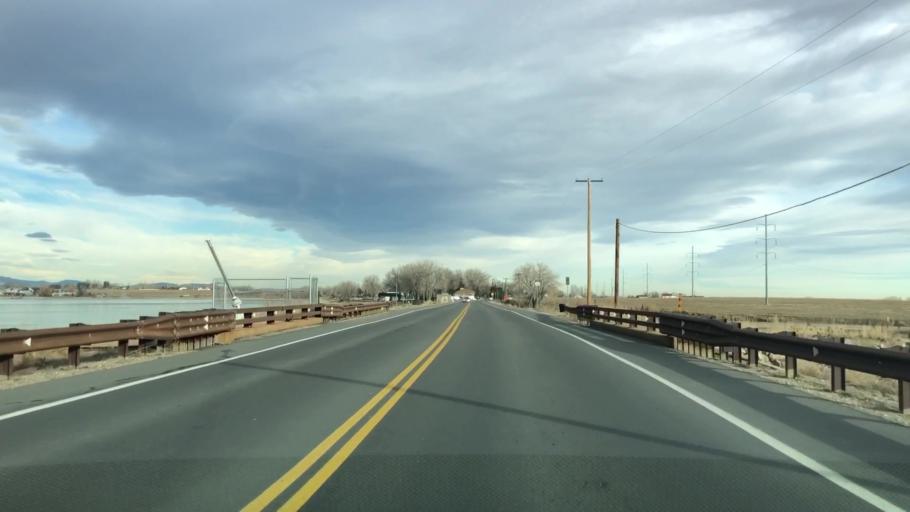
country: US
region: Colorado
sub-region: Larimer County
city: Loveland
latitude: 40.4387
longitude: -105.0455
